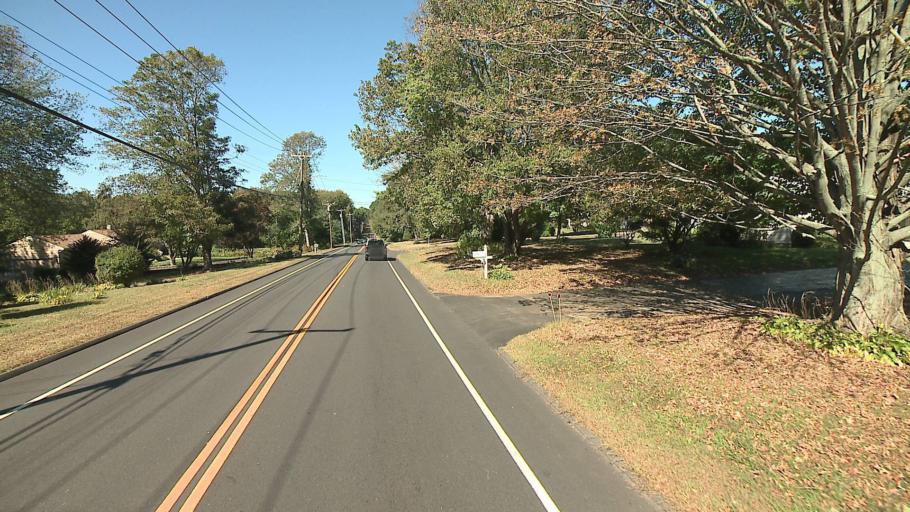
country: US
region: Connecticut
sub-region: New Haven County
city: Orange
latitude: 41.2870
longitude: -73.0122
